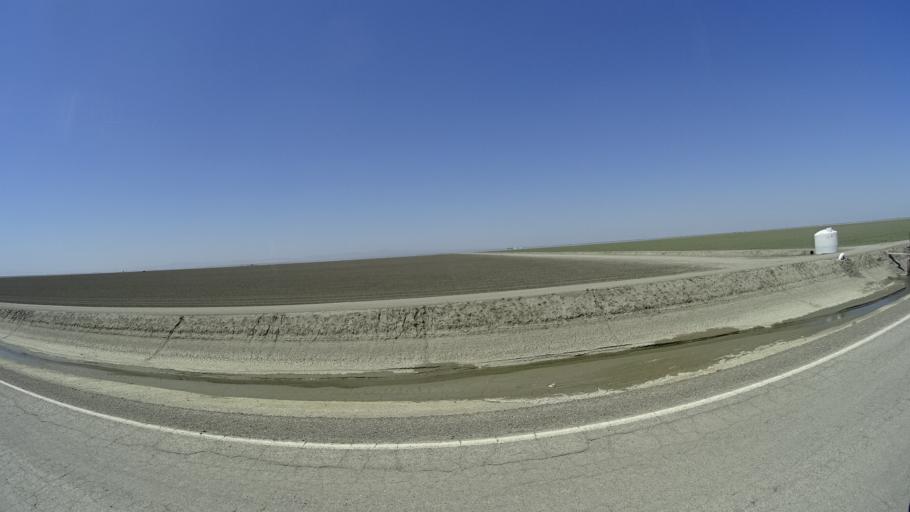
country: US
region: California
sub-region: Kings County
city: Corcoran
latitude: 36.0141
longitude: -119.6432
